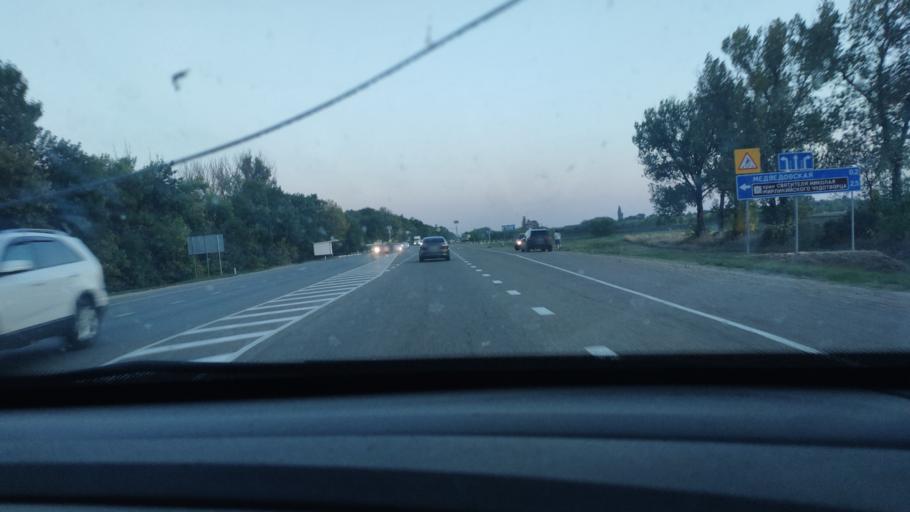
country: RU
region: Krasnodarskiy
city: Medvedovskaya
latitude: 45.4553
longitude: 38.9887
